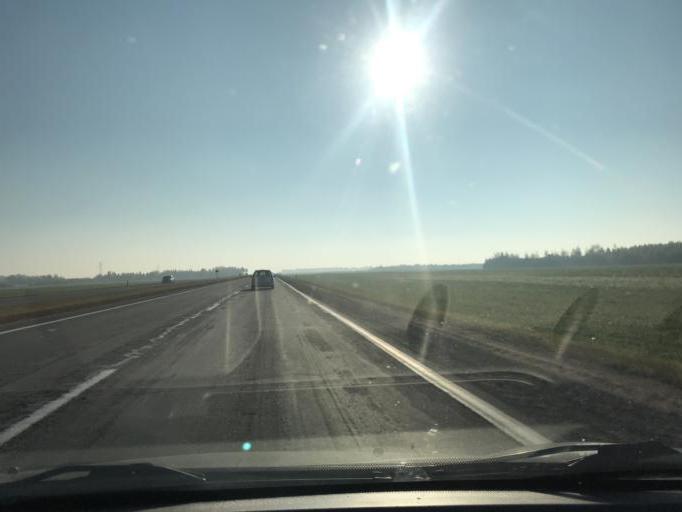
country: BY
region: Minsk
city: Dukora
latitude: 53.6496
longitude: 27.9752
